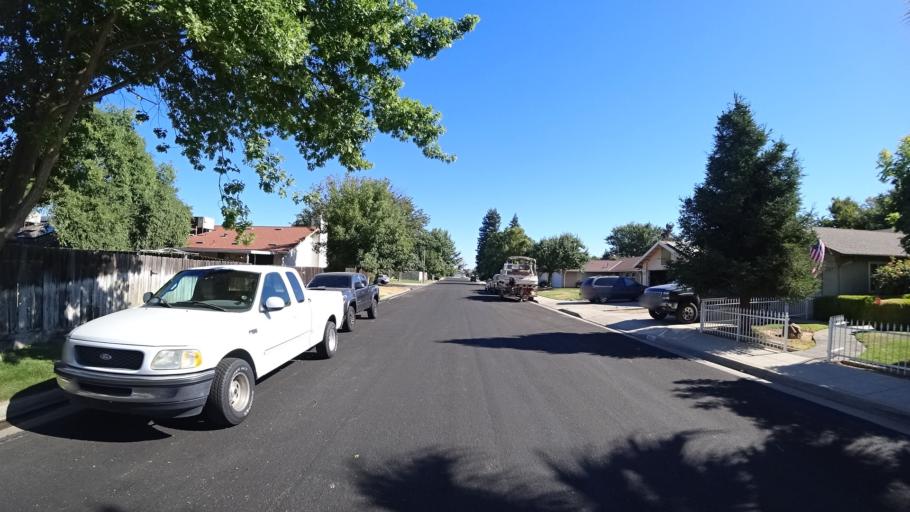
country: US
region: California
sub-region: Fresno County
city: West Park
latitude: 36.7844
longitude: -119.8581
